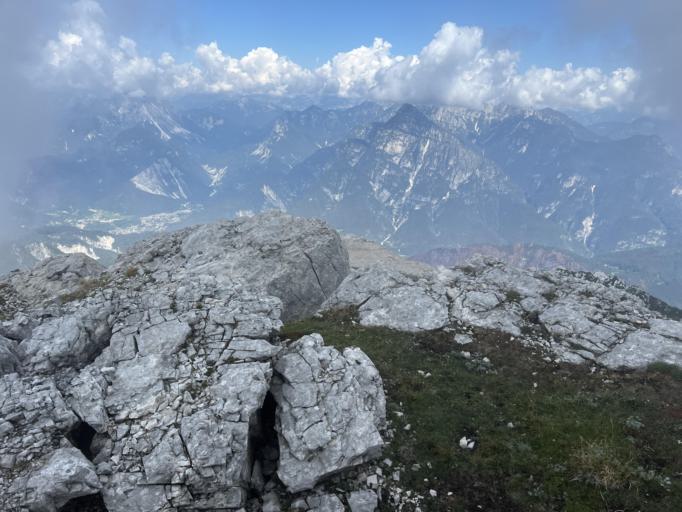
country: IT
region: Friuli Venezia Giulia
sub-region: Provincia di Udine
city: Resiutta
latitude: 46.3510
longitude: 13.2269
